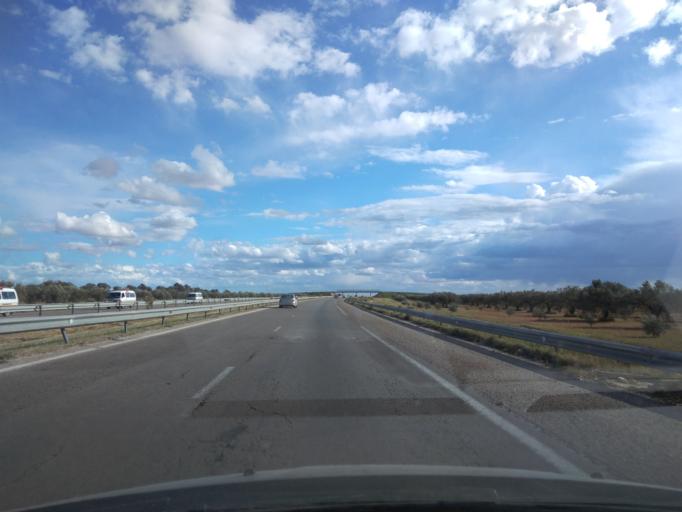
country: TN
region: Al Munastir
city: Manzil Kamil
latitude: 35.6240
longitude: 10.5930
